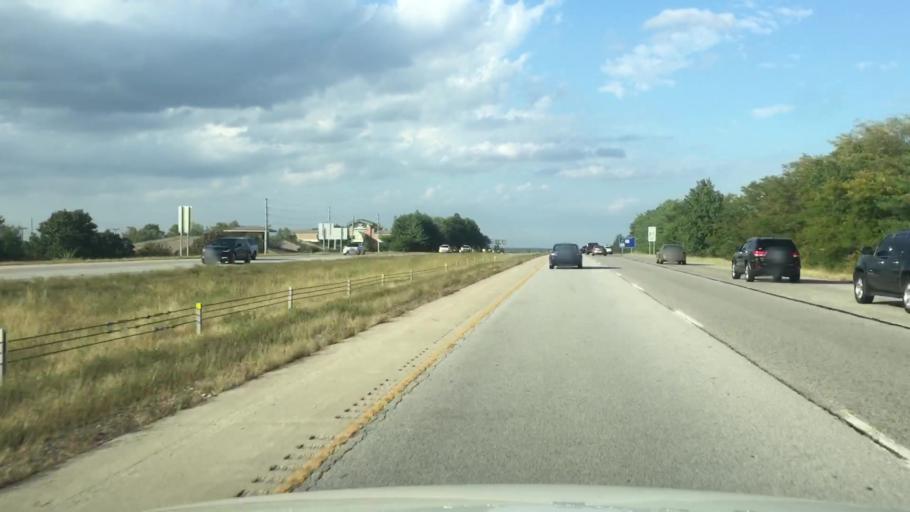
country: US
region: Missouri
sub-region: Jackson County
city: Lees Summit
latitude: 38.9744
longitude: -94.3572
